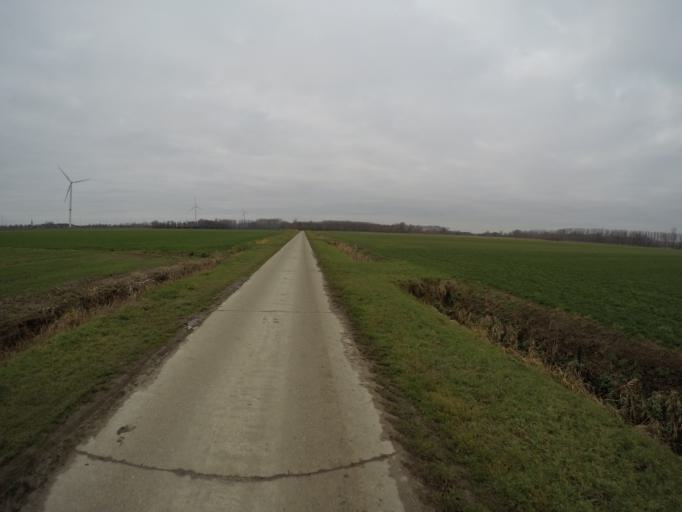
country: BE
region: Flanders
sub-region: Provincie Oost-Vlaanderen
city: Sint-Gillis-Waas
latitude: 51.2368
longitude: 4.1443
